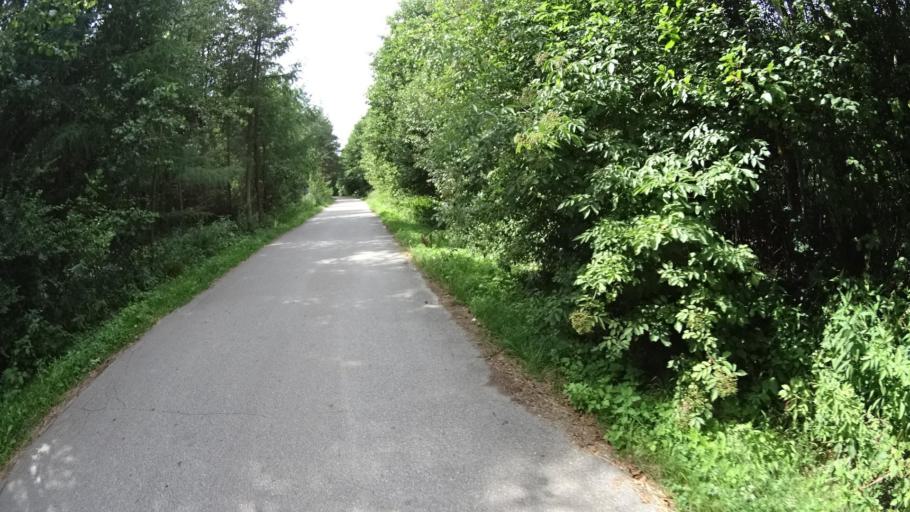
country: PL
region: Masovian Voivodeship
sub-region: Powiat bialobrzeski
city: Wysmierzyce
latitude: 51.6385
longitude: 20.8774
